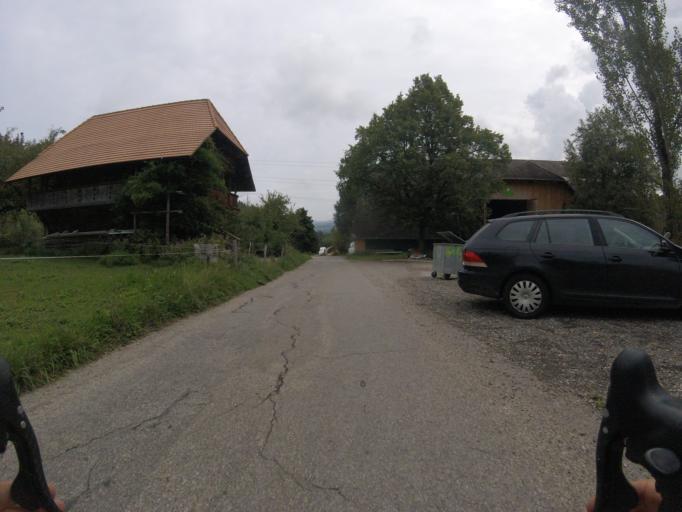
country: CH
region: Bern
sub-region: Emmental District
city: Lutzelfluh
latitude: 46.9745
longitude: 7.6775
